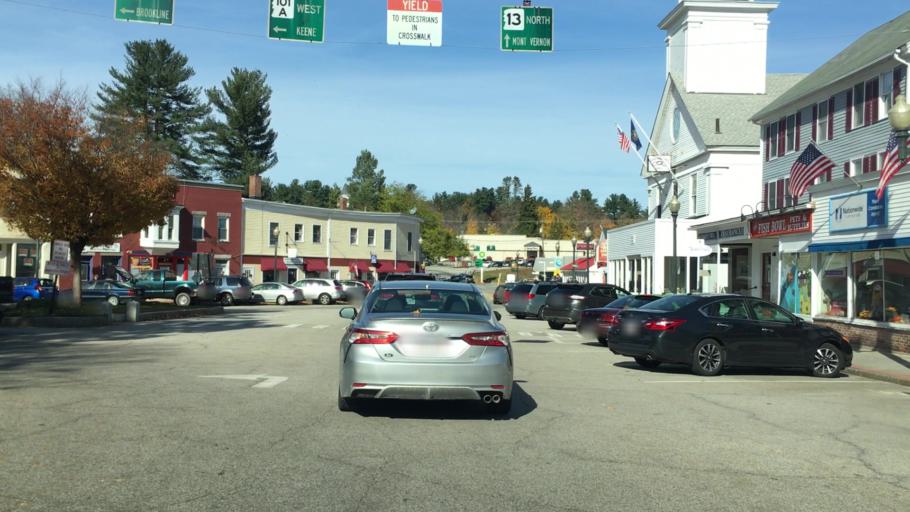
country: US
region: New Hampshire
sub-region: Hillsborough County
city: Milford
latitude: 42.8358
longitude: -71.6493
